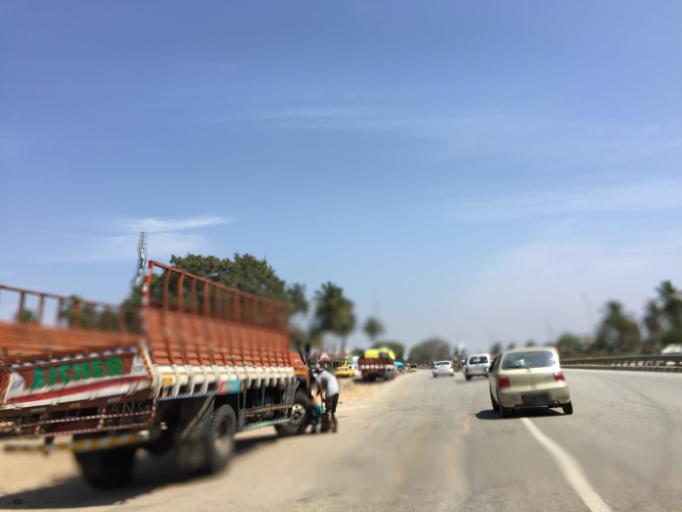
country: IN
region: Karnataka
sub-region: Kolar
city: Kolar
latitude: 13.1229
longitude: 78.1049
